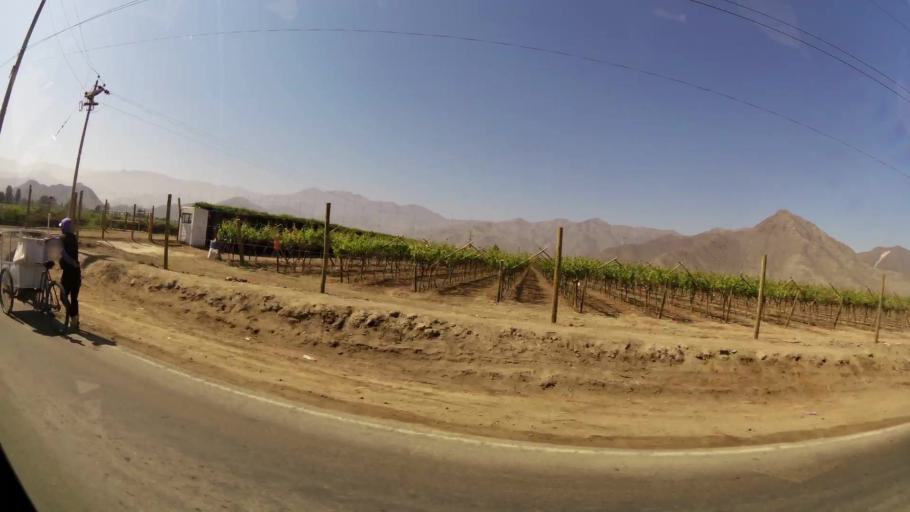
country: PE
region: Ica
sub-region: Provincia de Ica
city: San Juan Bautista
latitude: -13.9461
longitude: -75.6808
